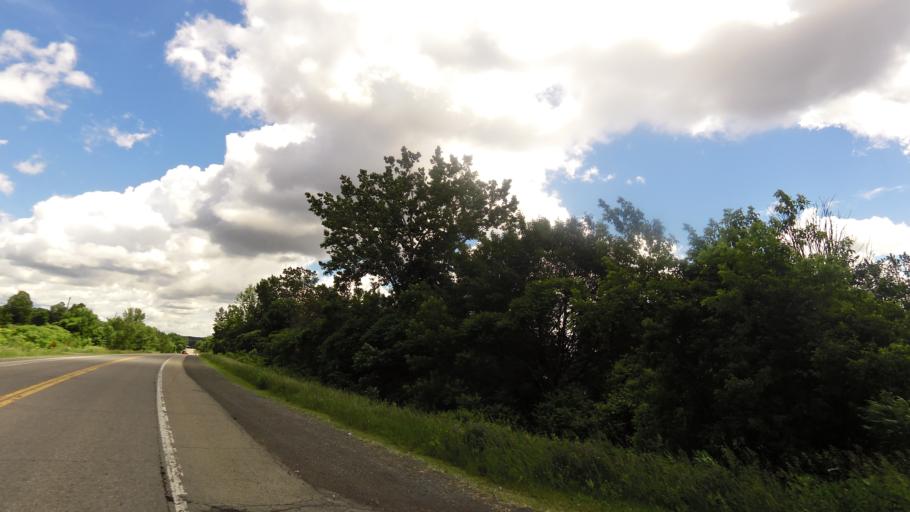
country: CA
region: Quebec
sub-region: Monteregie
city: Rigaud
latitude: 45.5293
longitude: -74.2728
